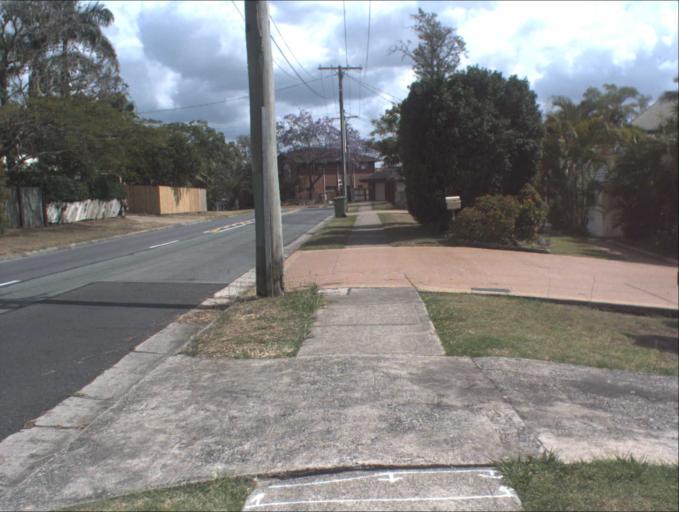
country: AU
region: Queensland
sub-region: Logan
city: Windaroo
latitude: -27.7217
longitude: 153.1937
